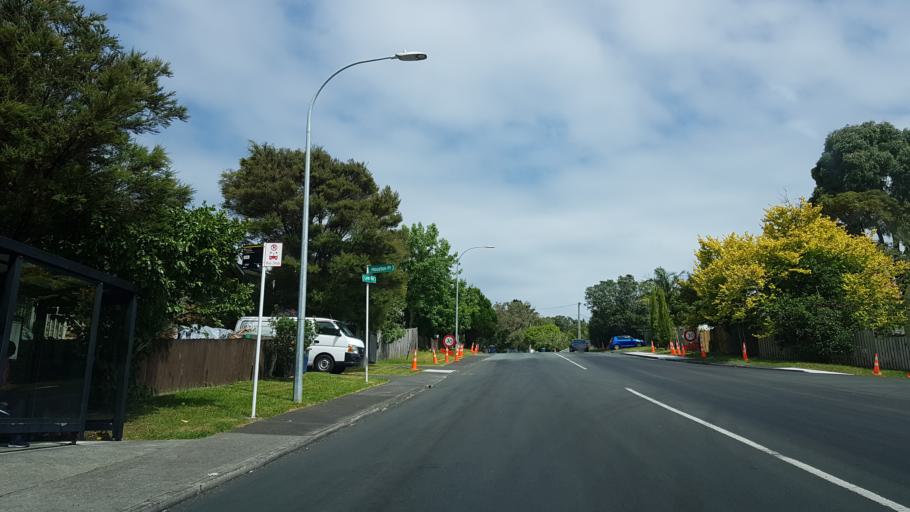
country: NZ
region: Auckland
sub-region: Auckland
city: North Shore
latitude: -36.7770
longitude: 174.7039
